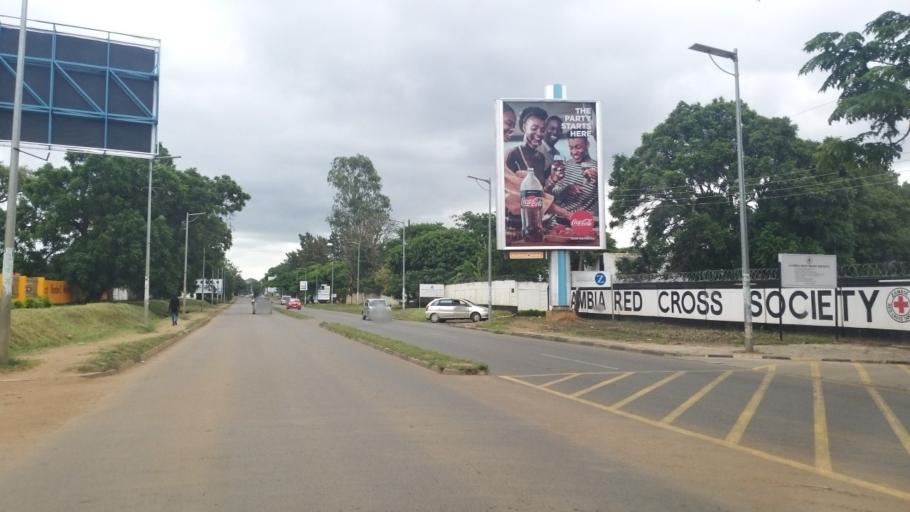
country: ZM
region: Lusaka
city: Lusaka
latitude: -15.4156
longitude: 28.3117
